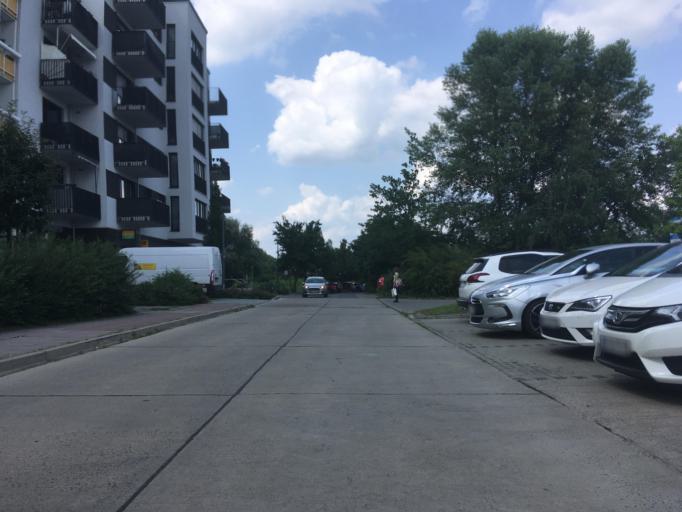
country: DE
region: Brandenburg
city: Wildau
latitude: 52.3252
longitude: 13.6230
